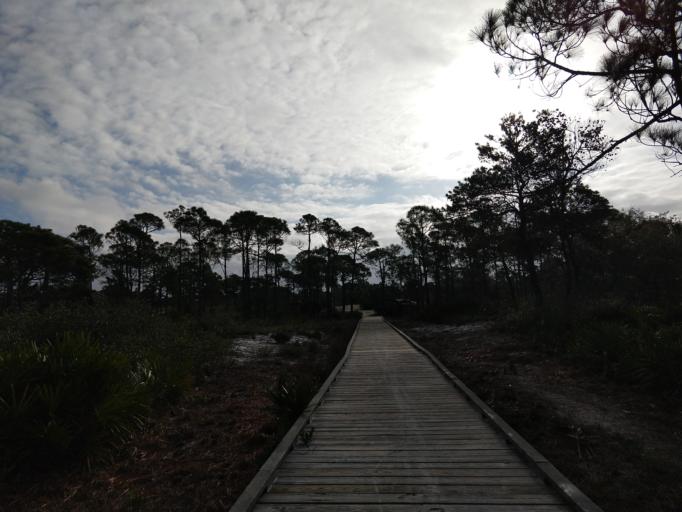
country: US
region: Florida
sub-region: Gulf County
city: Port Saint Joe
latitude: 29.7890
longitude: -85.4082
